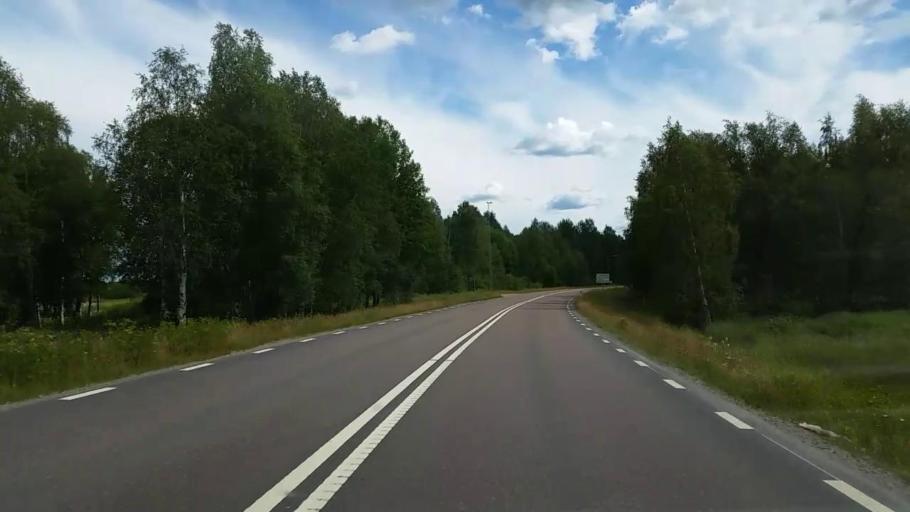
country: SE
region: Gaevleborg
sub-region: Ovanakers Kommun
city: Edsbyn
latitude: 61.3823
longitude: 15.8309
